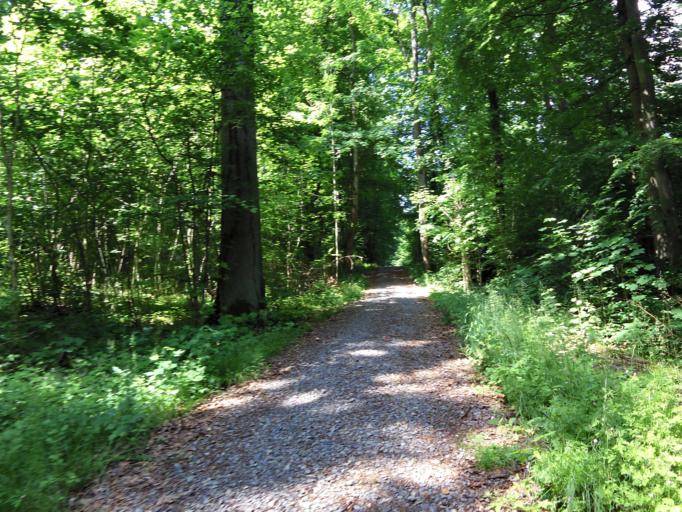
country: DE
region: Bavaria
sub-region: Regierungsbezirk Unterfranken
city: Wuerzburg
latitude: 49.7689
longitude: 9.8870
